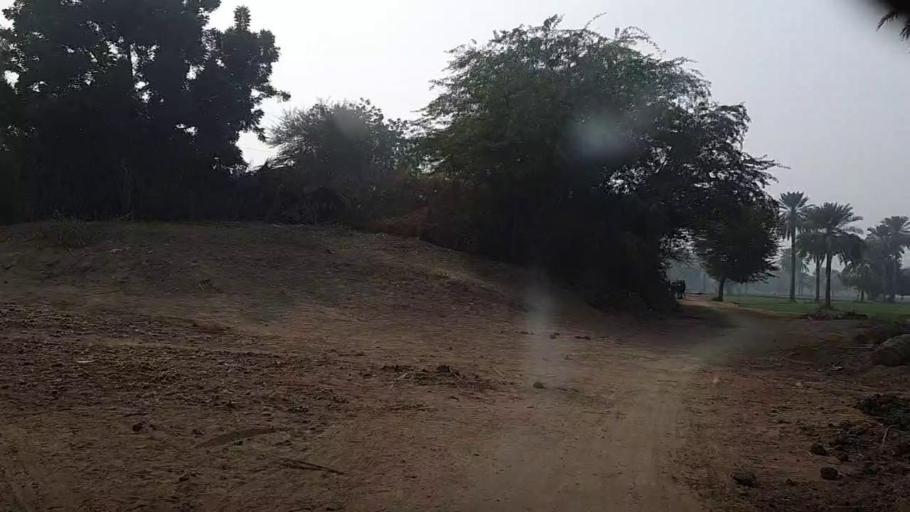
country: PK
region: Sindh
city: Bozdar
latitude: 27.0701
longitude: 68.6348
